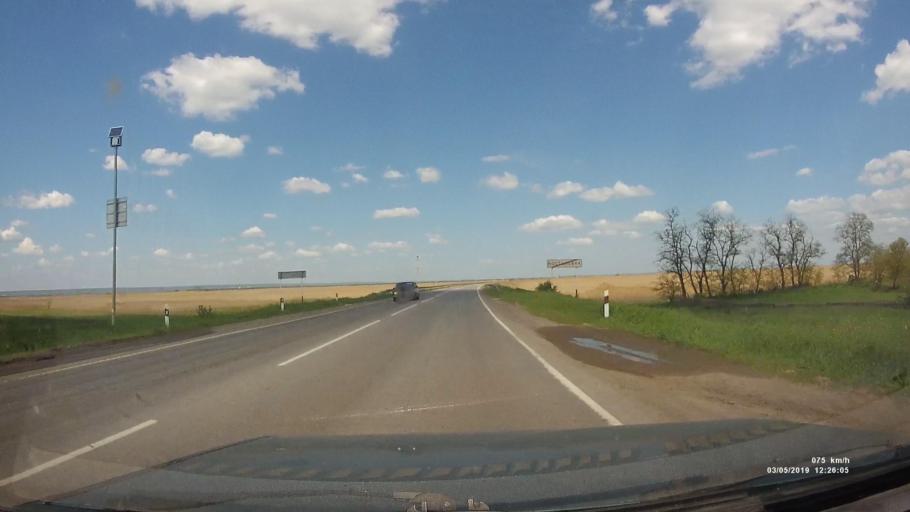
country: RU
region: Rostov
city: Semikarakorsk
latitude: 47.4407
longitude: 40.7121
